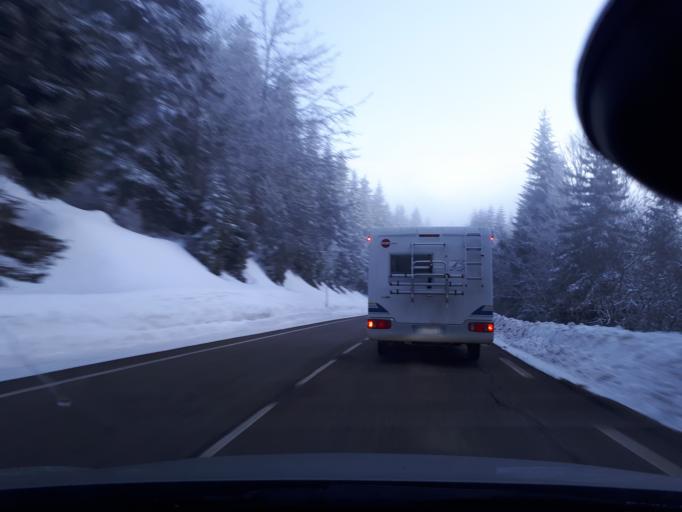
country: FR
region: Rhone-Alpes
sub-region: Departement de l'Isere
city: Vaulnaveys-le-Bas
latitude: 45.0987
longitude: 5.8596
